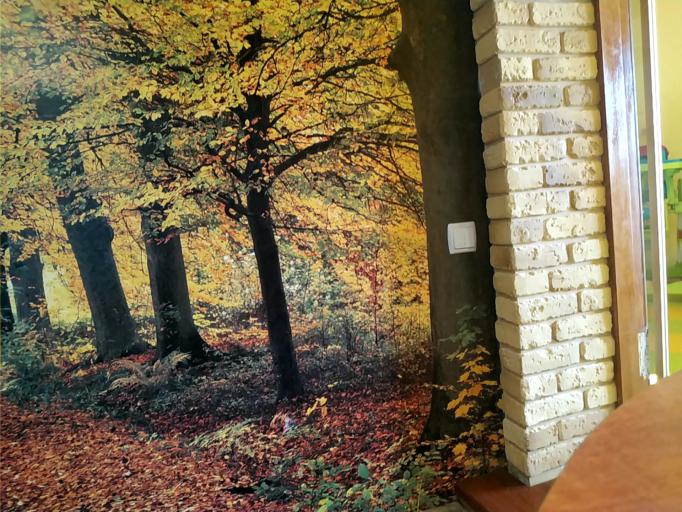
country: RU
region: Vologda
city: Nelazskoye
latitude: 59.4019
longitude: 37.6091
